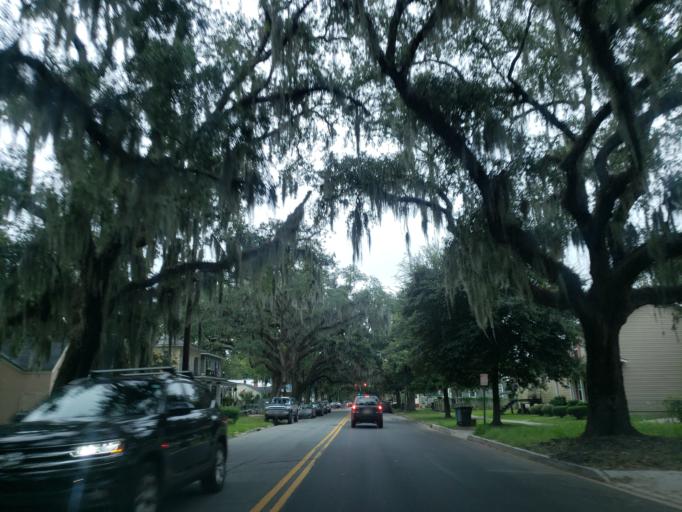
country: US
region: Georgia
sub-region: Chatham County
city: Savannah
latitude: 32.0542
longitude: -81.0890
